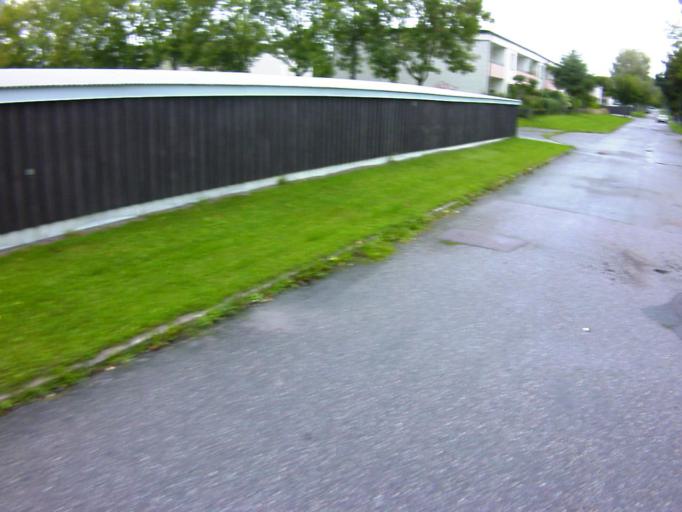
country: SE
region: Soedermanland
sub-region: Eskilstuna Kommun
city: Eskilstuna
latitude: 59.3851
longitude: 16.5373
